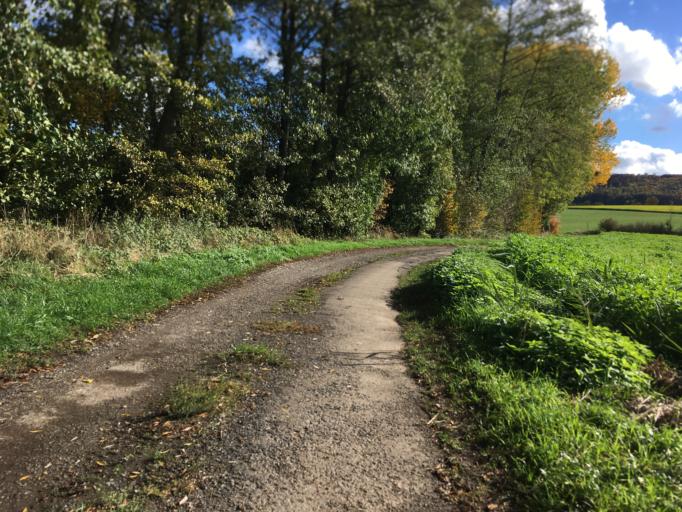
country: DE
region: Baden-Wuerttemberg
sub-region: Regierungsbezirk Stuttgart
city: Neuenstein
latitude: 49.1940
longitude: 9.5823
